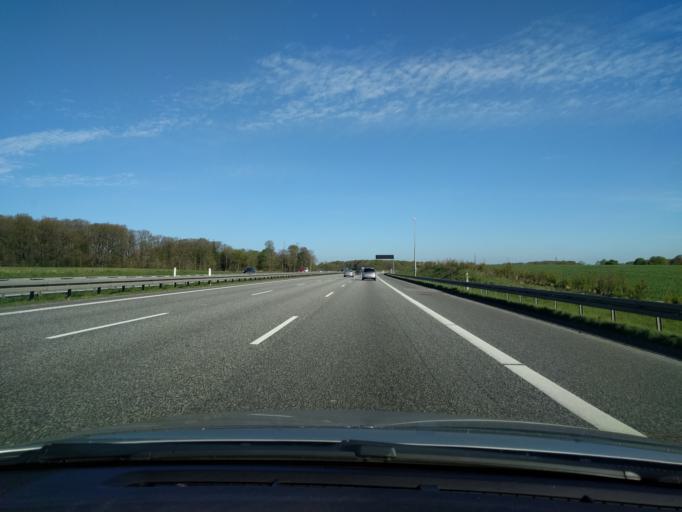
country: DK
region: South Denmark
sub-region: Vejle Kommune
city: Borkop
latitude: 55.6236
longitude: 9.5715
